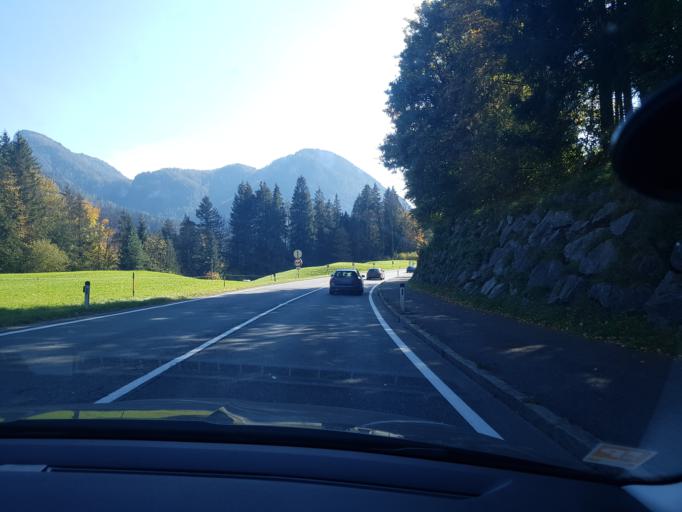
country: AT
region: Salzburg
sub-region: Politischer Bezirk Zell am See
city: Lofer
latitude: 47.6046
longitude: 12.7021
